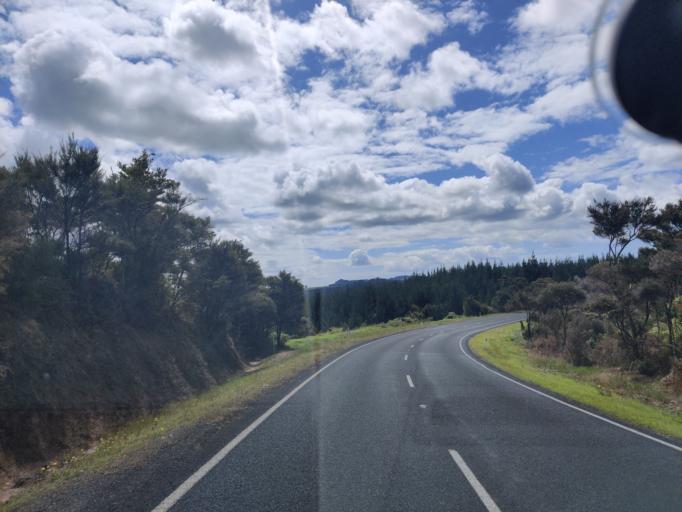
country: NZ
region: Northland
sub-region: Far North District
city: Kerikeri
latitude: -35.1348
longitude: 173.8767
